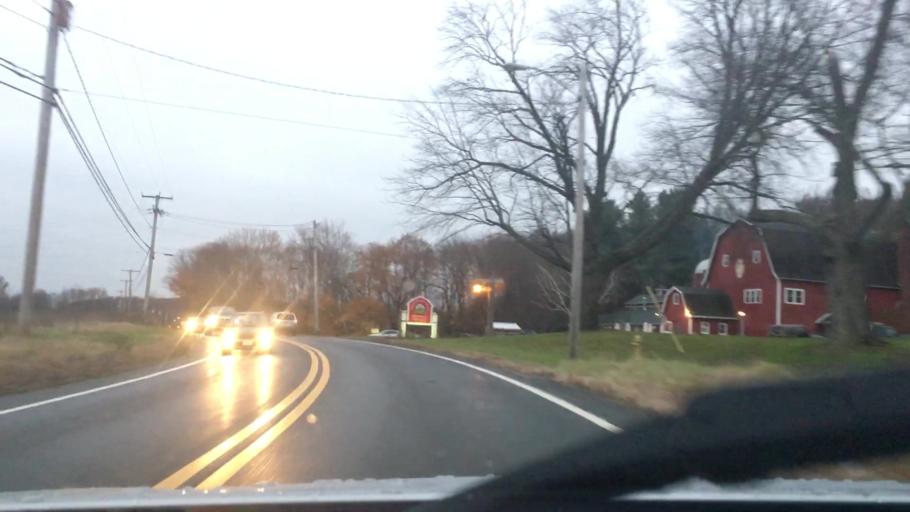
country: US
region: Massachusetts
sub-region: Hampden County
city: Southwick
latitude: 42.0753
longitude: -72.7686
